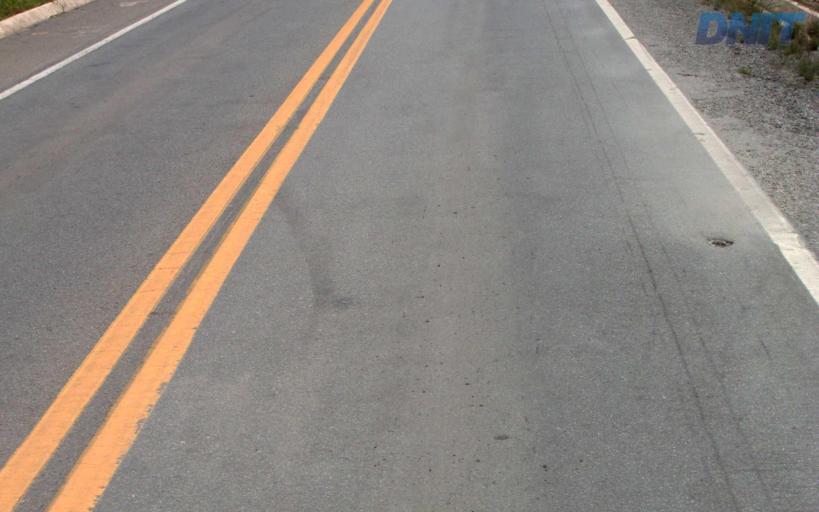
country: BR
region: Minas Gerais
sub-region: Governador Valadares
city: Governador Valadares
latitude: -19.0636
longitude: -42.1631
